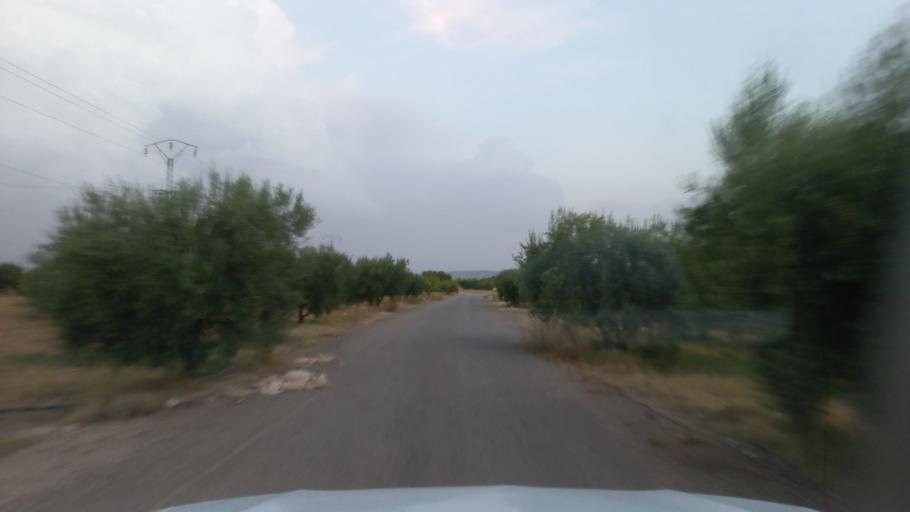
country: TN
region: Al Qasrayn
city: Kasserine
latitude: 35.2716
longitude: 9.0371
